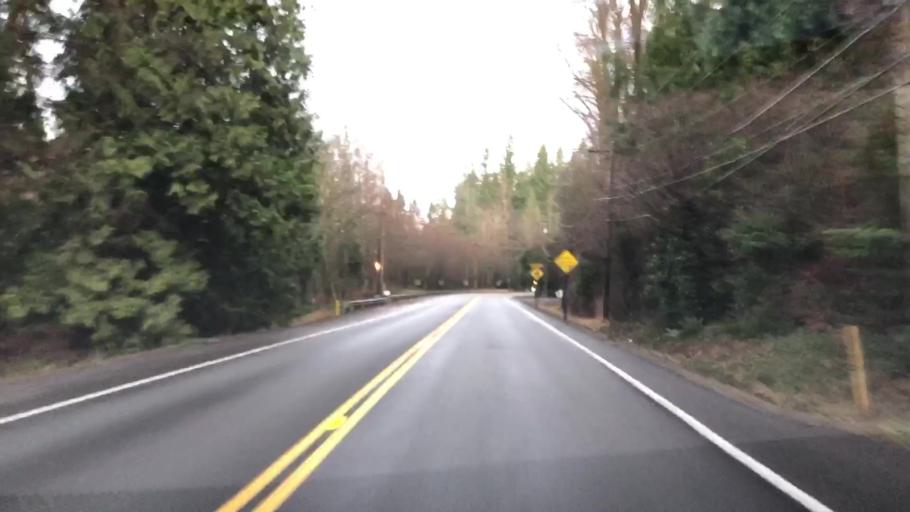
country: US
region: Washington
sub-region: King County
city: Cottage Lake
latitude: 47.7582
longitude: -122.0403
